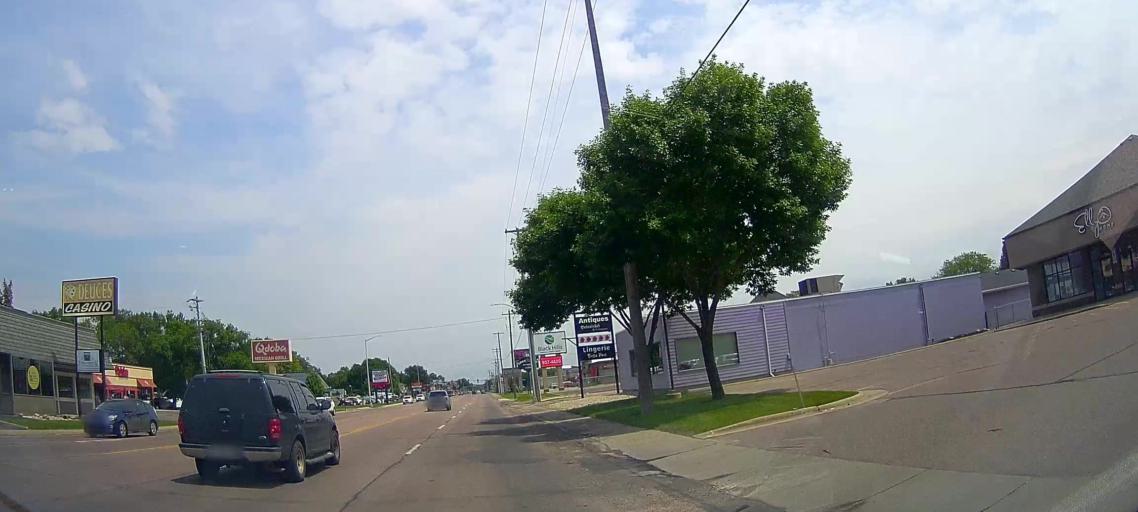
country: US
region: South Dakota
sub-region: Minnehaha County
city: Sioux Falls
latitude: 43.5147
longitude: -96.7501
